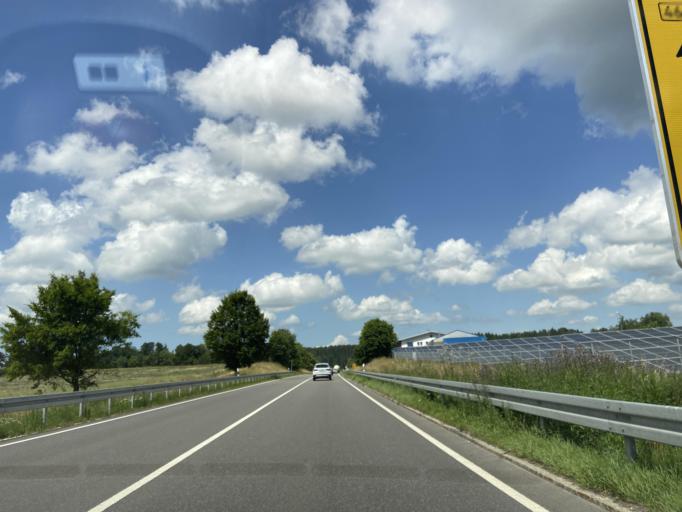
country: DE
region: Baden-Wuerttemberg
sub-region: Tuebingen Region
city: Strassberg
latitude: 48.1790
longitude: 9.1035
